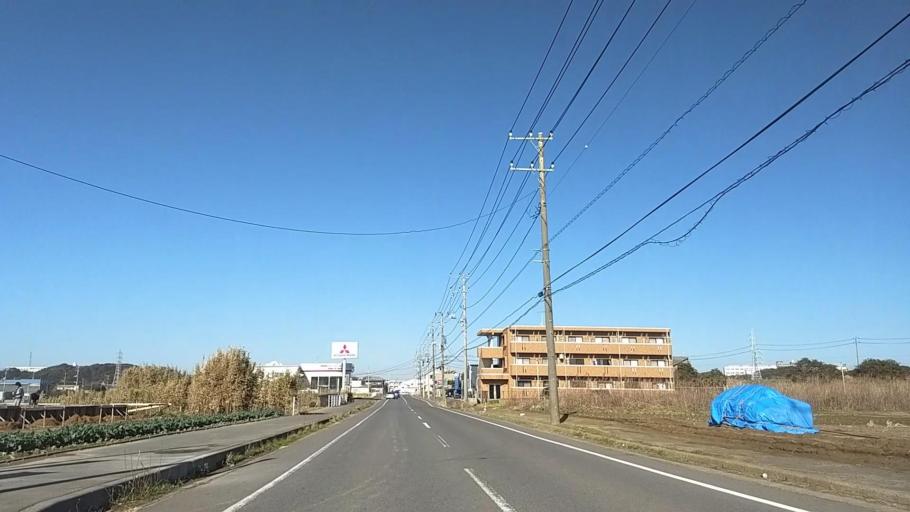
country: JP
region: Chiba
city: Hasaki
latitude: 35.7158
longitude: 140.8391
